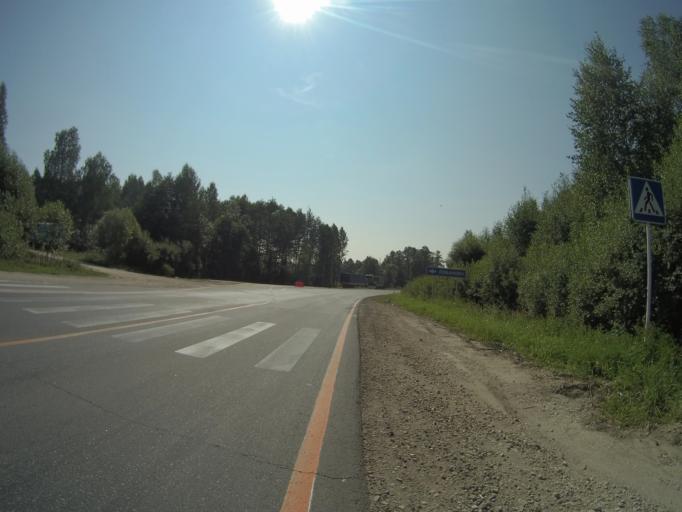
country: RU
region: Vladimir
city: Anopino
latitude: 55.8532
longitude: 40.6439
